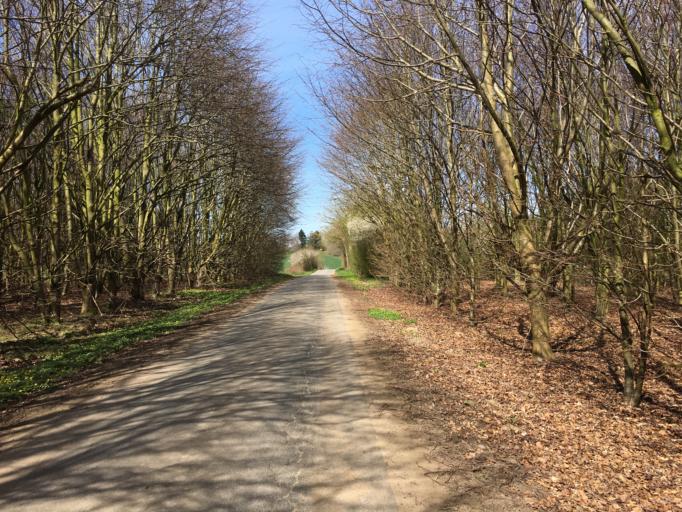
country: DE
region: Schleswig-Holstein
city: Nottfeld
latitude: 54.5902
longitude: 9.8004
